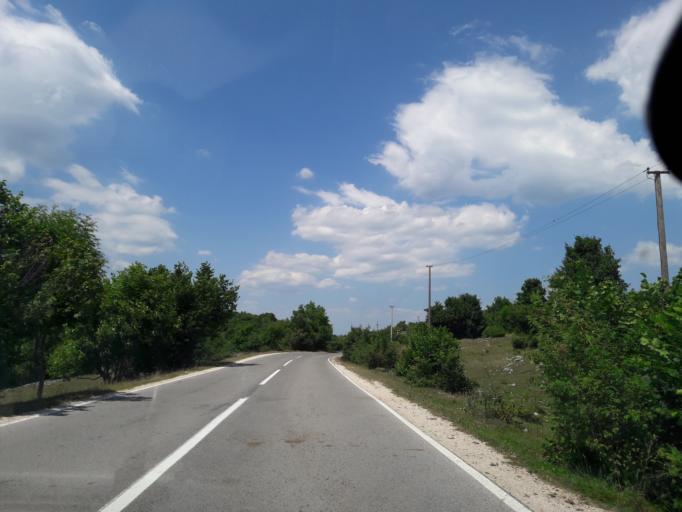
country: BA
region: Republika Srpska
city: Sipovo
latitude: 44.1395
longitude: 17.1798
